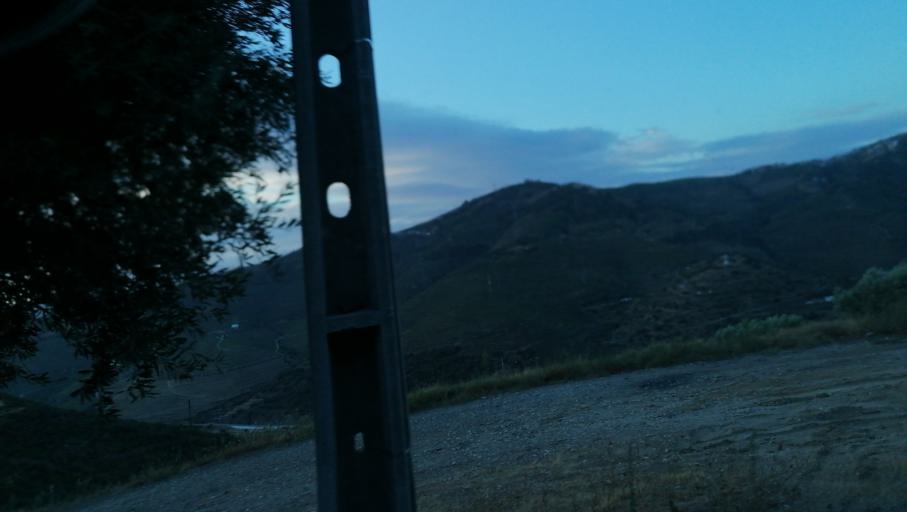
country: PT
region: Vila Real
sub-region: Peso da Regua
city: Peso da Regua
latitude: 41.1408
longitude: -7.7445
